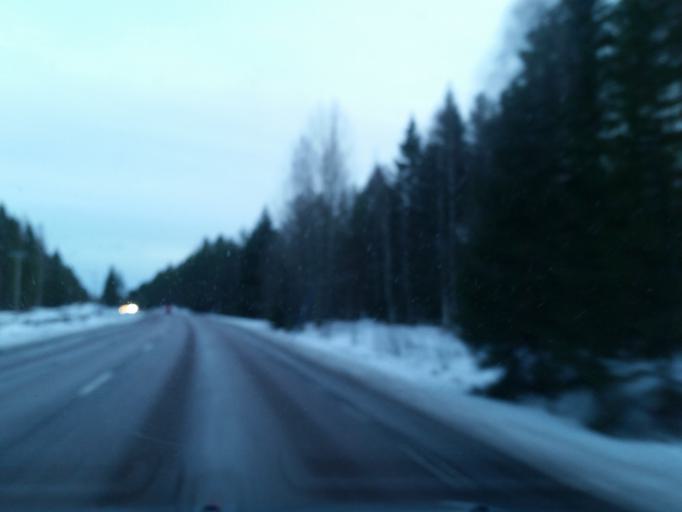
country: SE
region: Gaevleborg
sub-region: Sandvikens Kommun
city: Sandviken
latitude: 60.6533
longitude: 16.7212
